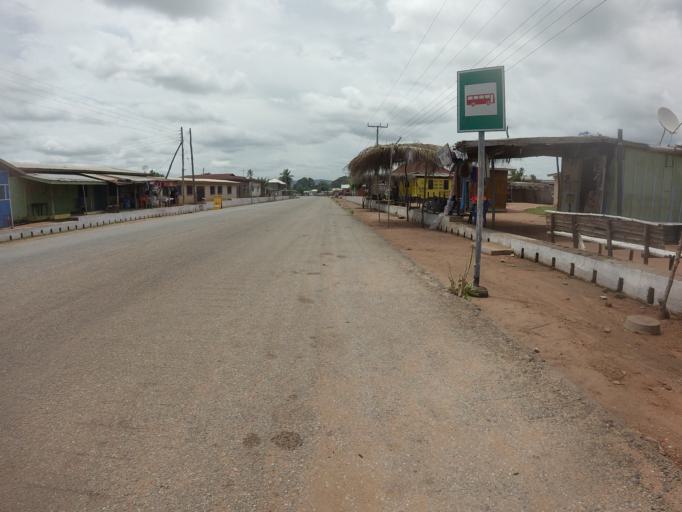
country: GH
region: Volta
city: Ho
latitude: 6.5736
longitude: 0.3813
